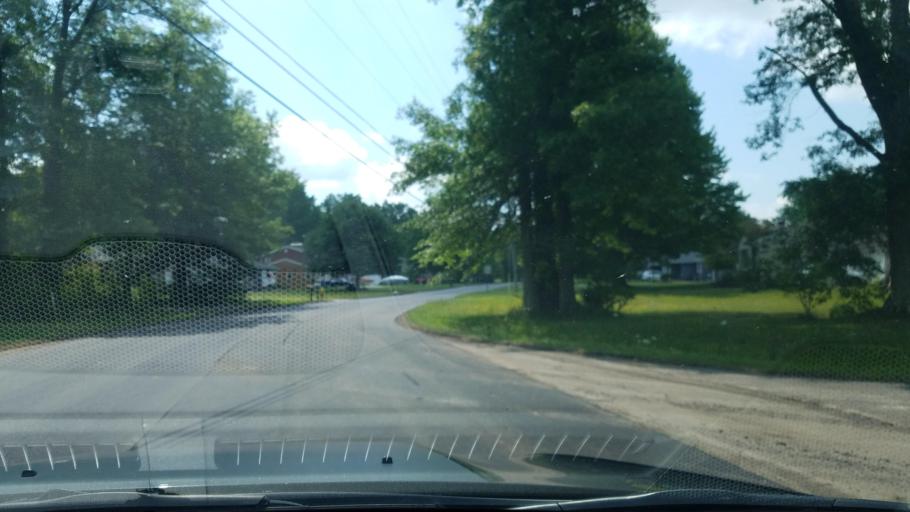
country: US
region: Ohio
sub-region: Trumbull County
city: Champion Heights
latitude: 41.3031
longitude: -80.8640
